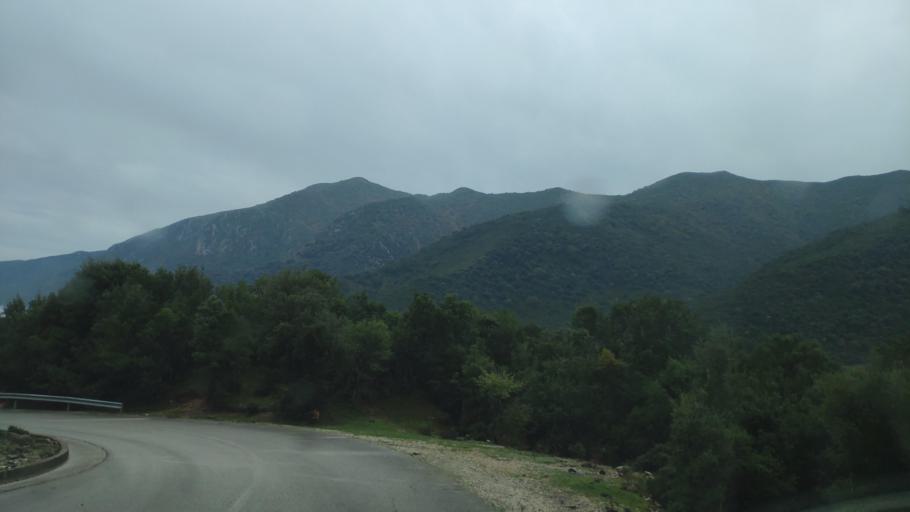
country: GR
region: Epirus
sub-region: Nomos Thesprotias
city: Paramythia
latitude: 39.3953
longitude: 20.6238
